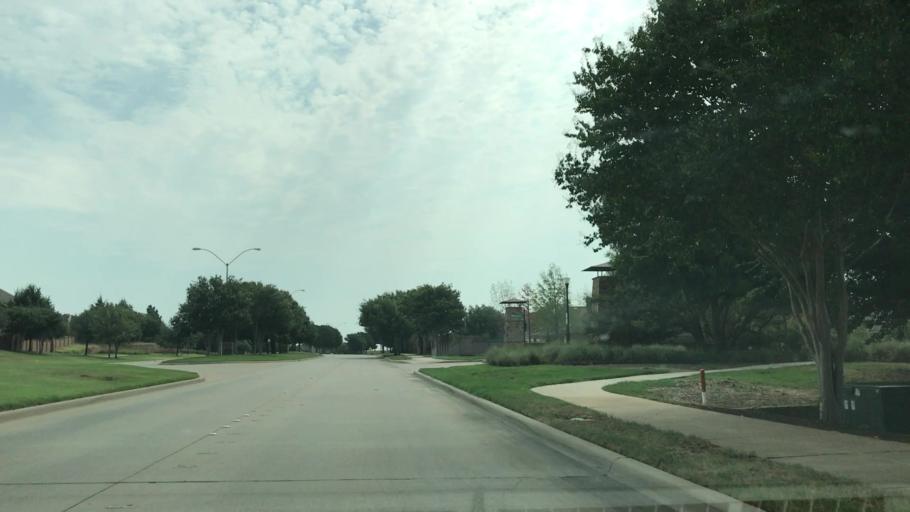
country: US
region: Texas
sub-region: Tarrant County
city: Keller
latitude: 32.9103
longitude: -97.2771
